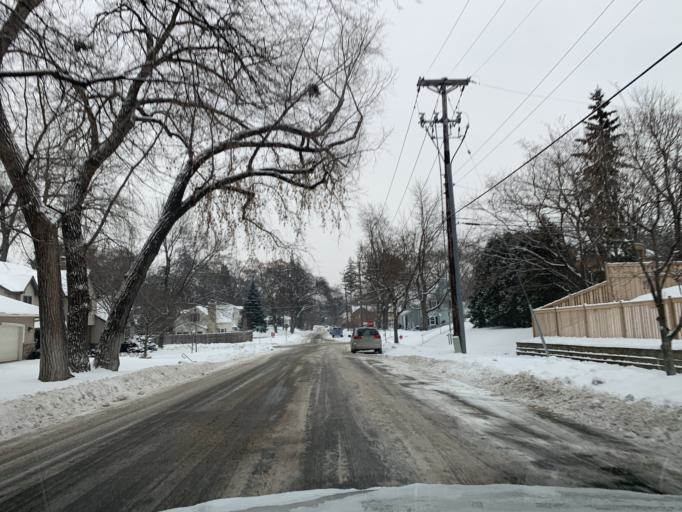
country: US
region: Minnesota
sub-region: Hennepin County
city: Saint Louis Park
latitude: 44.9521
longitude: -93.3336
